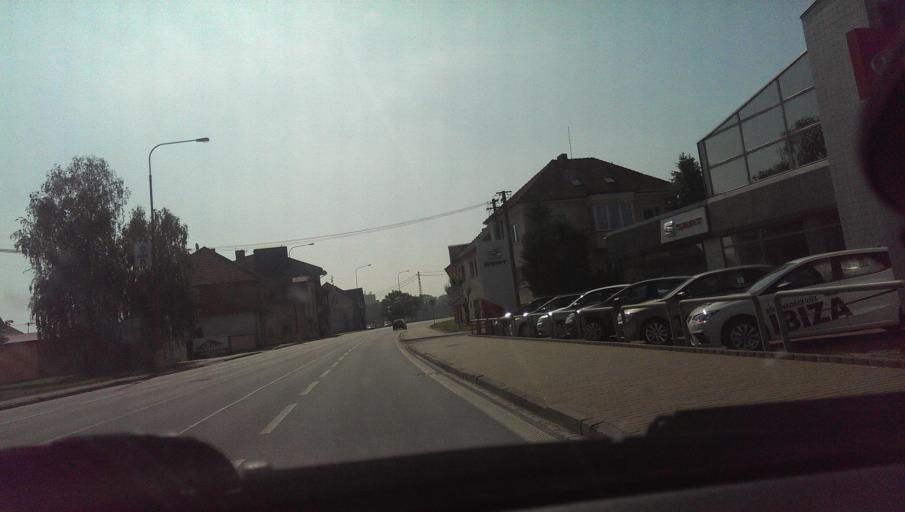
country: CZ
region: Zlin
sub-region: Okres Uherske Hradiste
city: Uherske Hradiste
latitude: 49.0746
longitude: 17.4569
